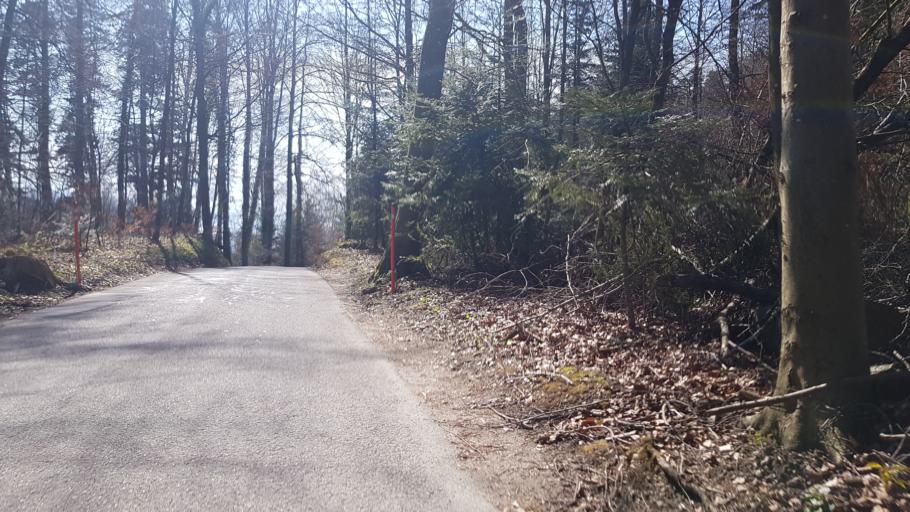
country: CH
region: Aargau
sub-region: Bezirk Kulm
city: Reinach
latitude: 47.2812
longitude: 8.1874
